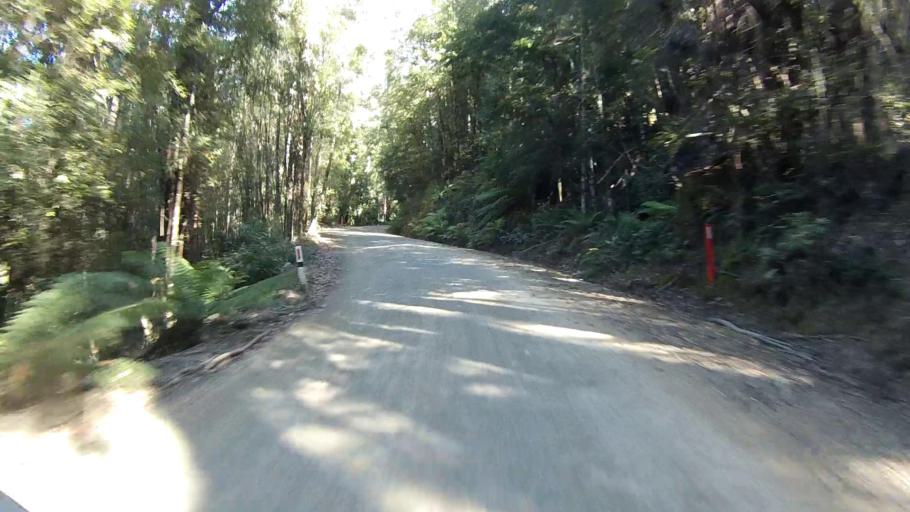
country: AU
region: Tasmania
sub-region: Derwent Valley
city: New Norfolk
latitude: -42.6762
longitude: 146.6960
